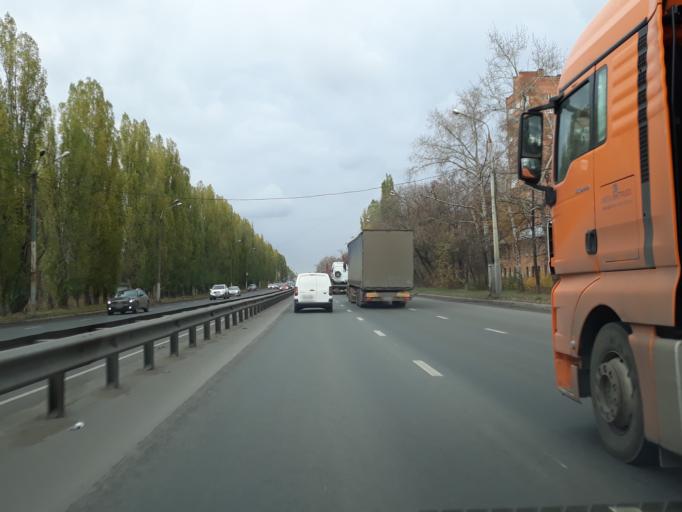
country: RU
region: Nizjnij Novgorod
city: Nizhniy Novgorod
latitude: 56.2723
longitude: 43.9089
